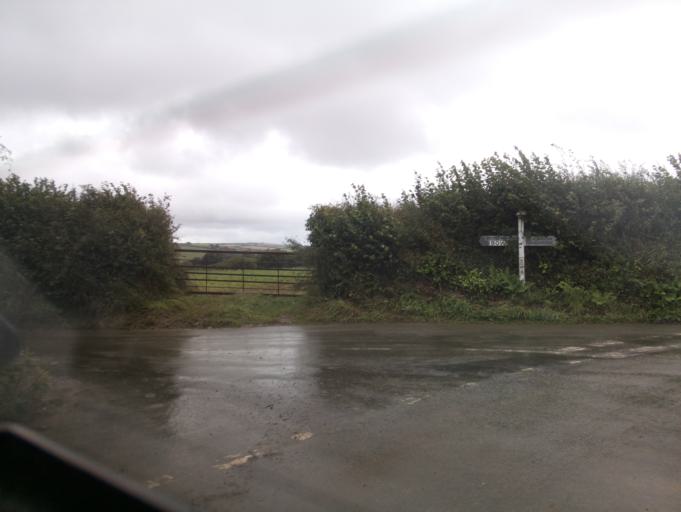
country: GB
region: England
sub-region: Devon
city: Totnes
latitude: 50.3281
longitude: -3.6821
